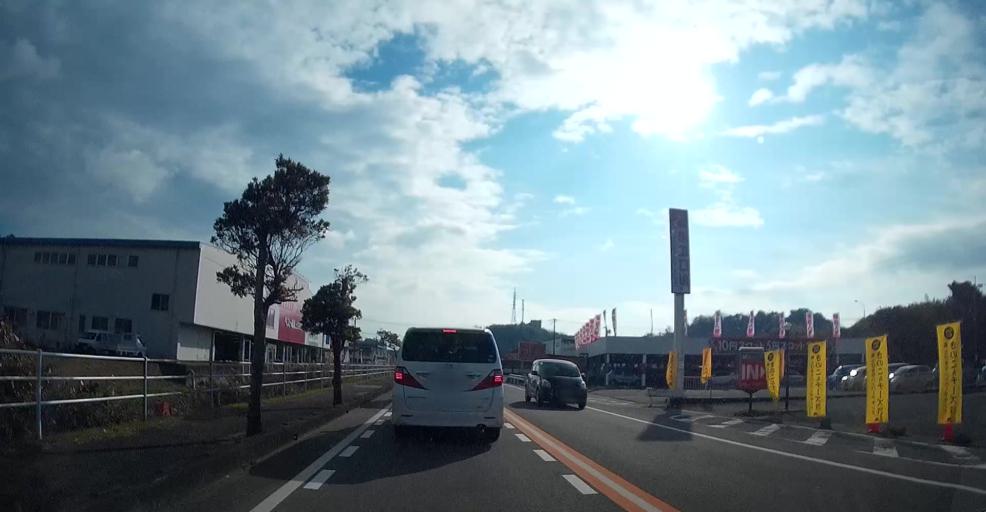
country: JP
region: Kumamoto
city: Yatsushiro
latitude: 32.5914
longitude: 130.4300
